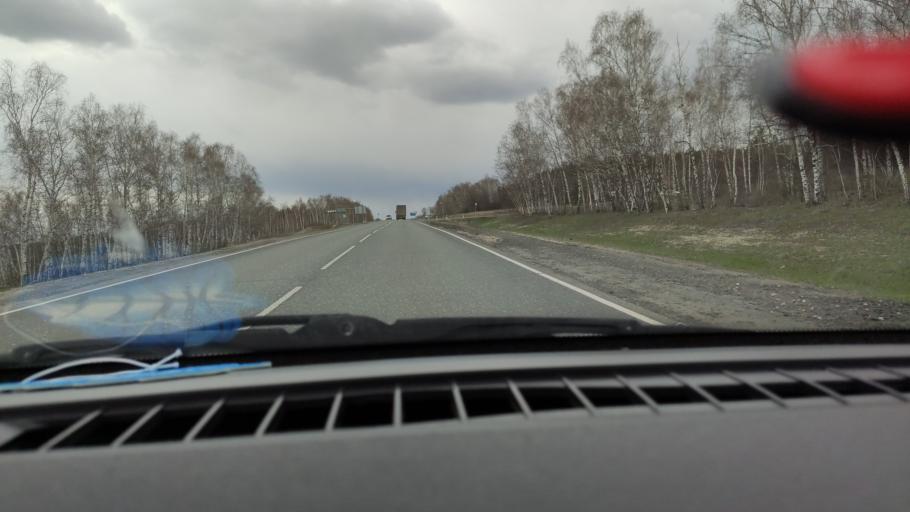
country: RU
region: Saratov
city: Sennoy
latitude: 52.1174
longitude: 46.8401
